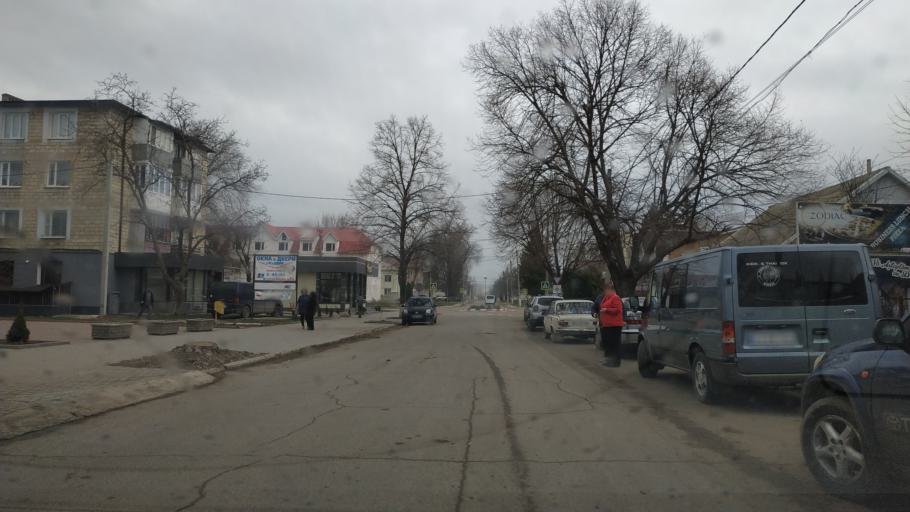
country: MD
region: Leova
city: Leova
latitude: 46.4833
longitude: 28.2512
